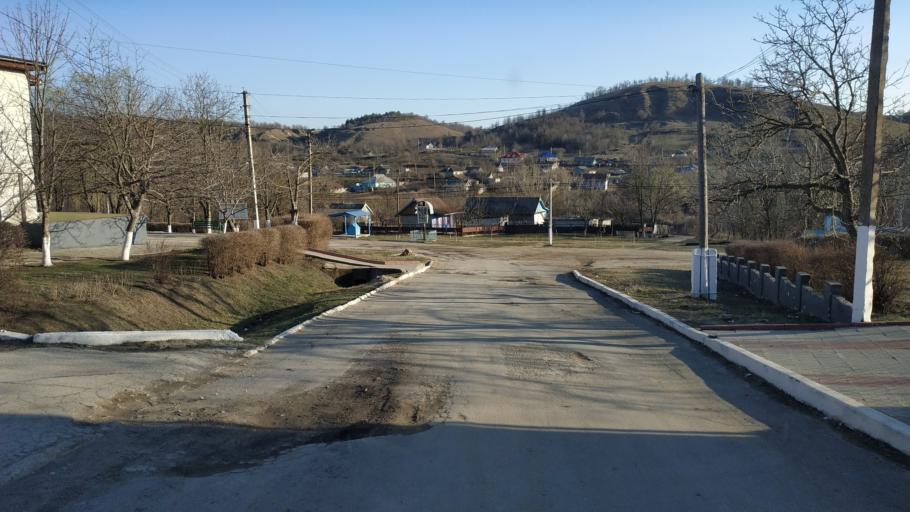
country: MD
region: Hincesti
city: Hincesti
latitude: 46.6993
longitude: 28.5443
